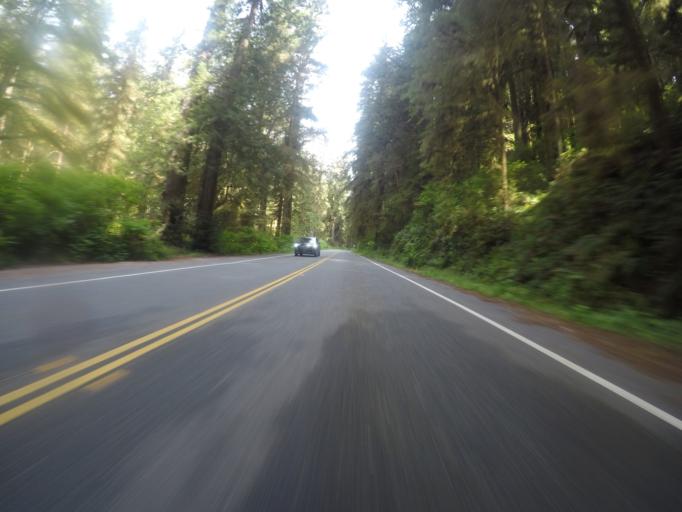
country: US
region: California
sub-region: Del Norte County
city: Bertsch-Oceanview
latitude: 41.4275
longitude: -124.0370
